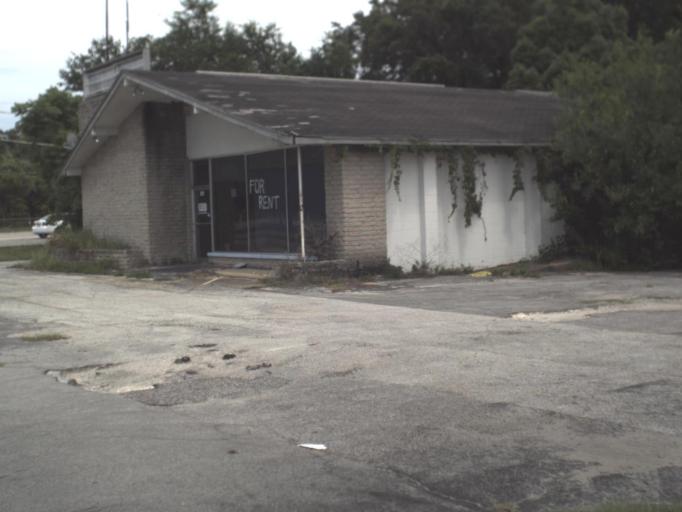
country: US
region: Florida
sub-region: Putnam County
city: Palatka
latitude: 29.6418
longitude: -81.6570
